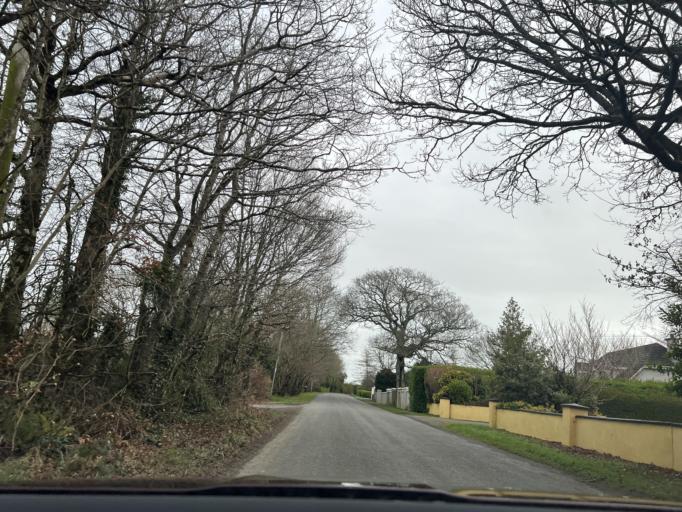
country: IE
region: Leinster
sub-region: Loch Garman
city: Castlebridge
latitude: 52.3819
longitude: -6.5323
